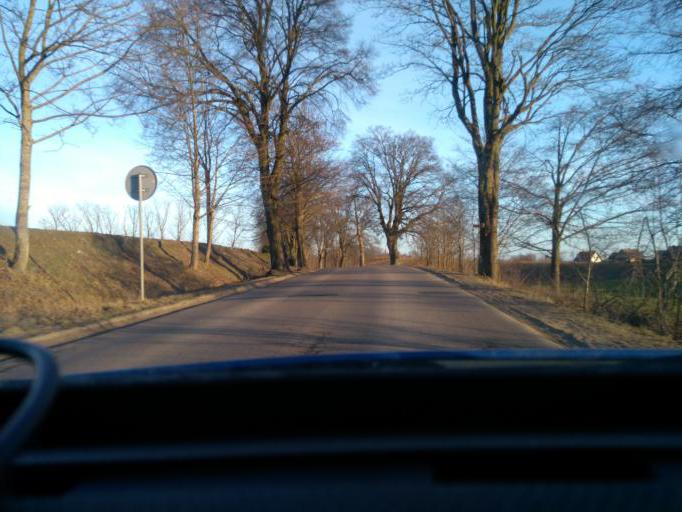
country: PL
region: Pomeranian Voivodeship
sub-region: Powiat kartuski
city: Przodkowo
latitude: 54.3870
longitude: 18.2701
